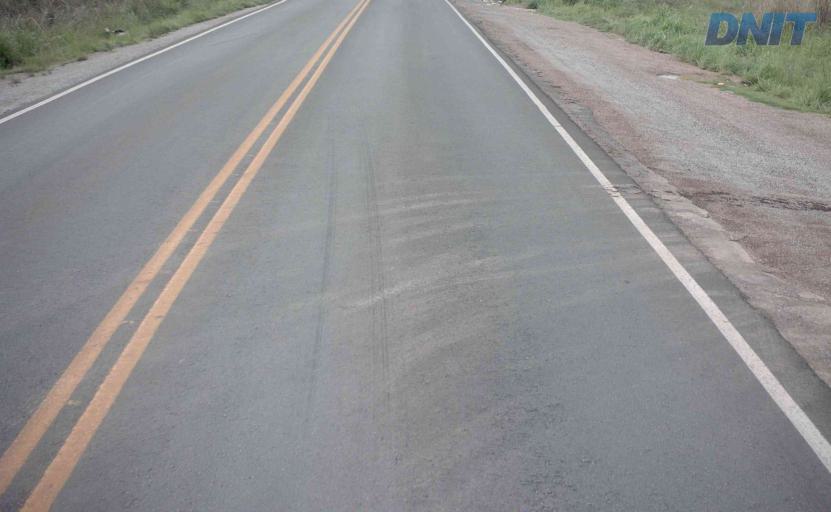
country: BR
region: Goias
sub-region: Padre Bernardo
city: Padre Bernardo
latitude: -15.2100
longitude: -48.2819
